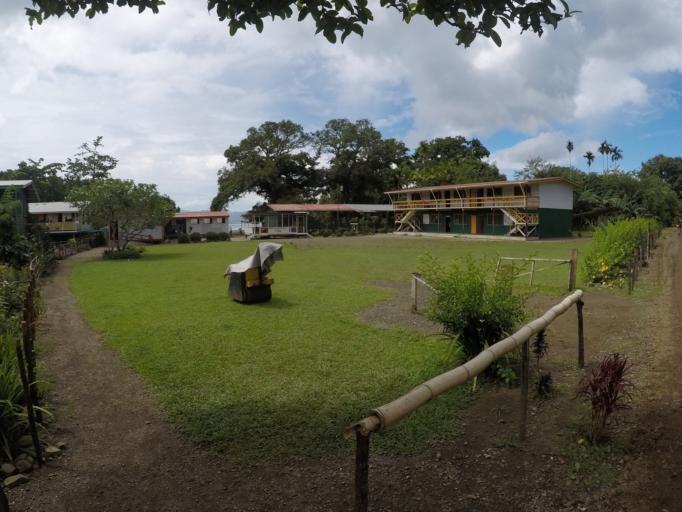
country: PG
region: Milne Bay
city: Alotau
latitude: -10.3455
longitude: 150.5953
